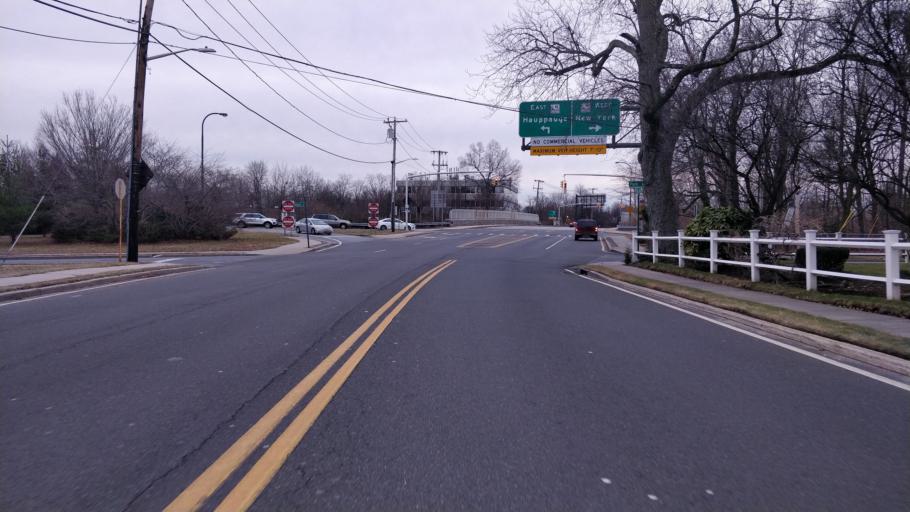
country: US
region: New York
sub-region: Nassau County
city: Westbury
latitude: 40.7648
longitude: -73.5870
